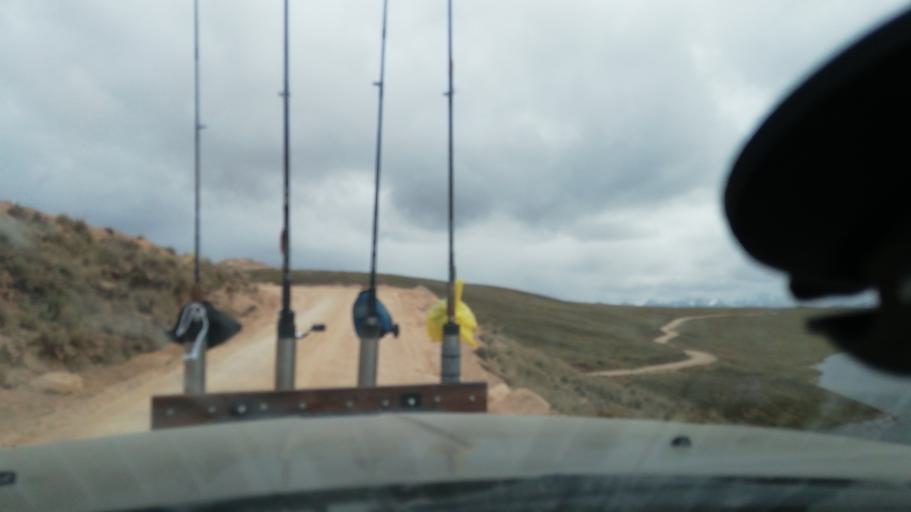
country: PE
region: Huancavelica
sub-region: Provincia de Huancavelica
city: Acobambilla
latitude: -12.5788
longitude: -75.5349
